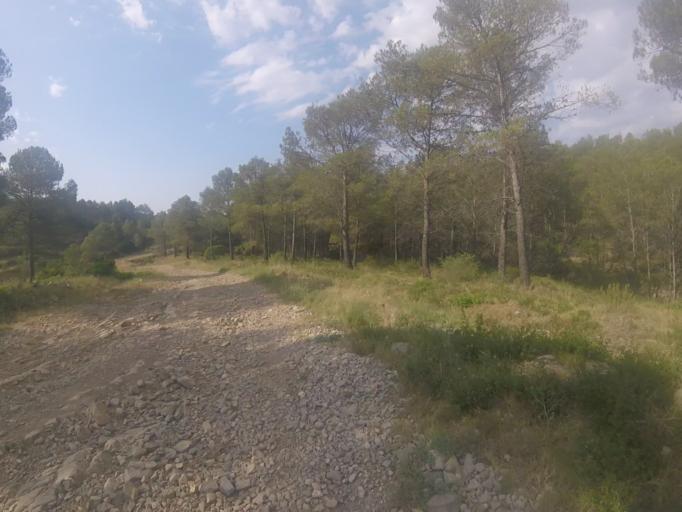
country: ES
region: Valencia
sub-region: Provincia de Castello
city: Cervera del Maestre
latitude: 40.3993
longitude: 0.2055
